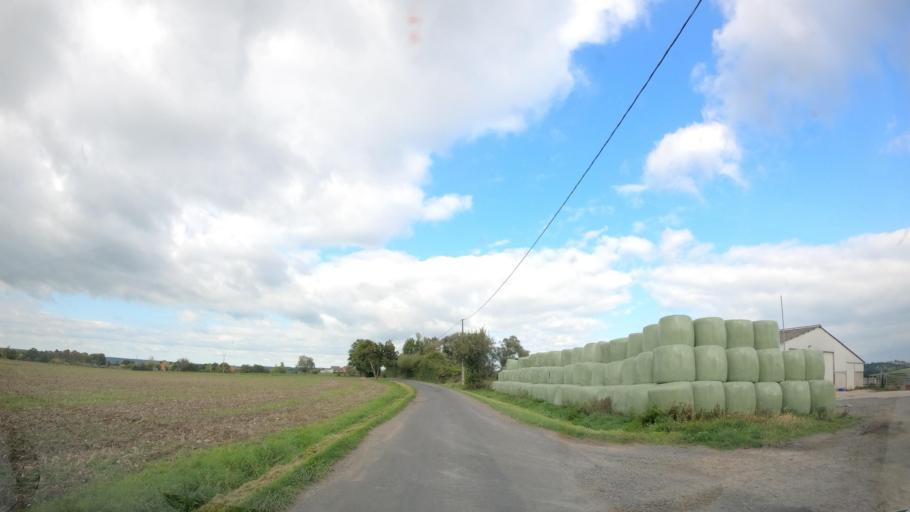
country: FR
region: Auvergne
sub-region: Departement de l'Allier
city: Lapalisse
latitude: 46.3604
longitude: 3.6203
